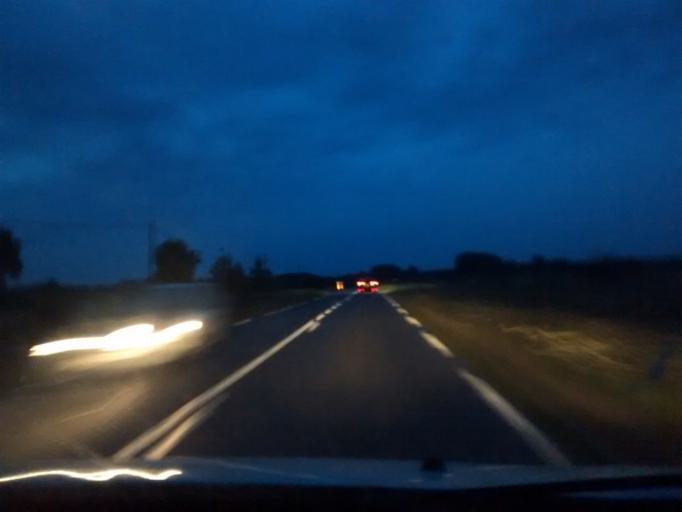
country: FR
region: Pays de la Loire
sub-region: Departement de la Loire-Atlantique
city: Fay-de-Bretagne
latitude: 47.4457
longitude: -1.8097
